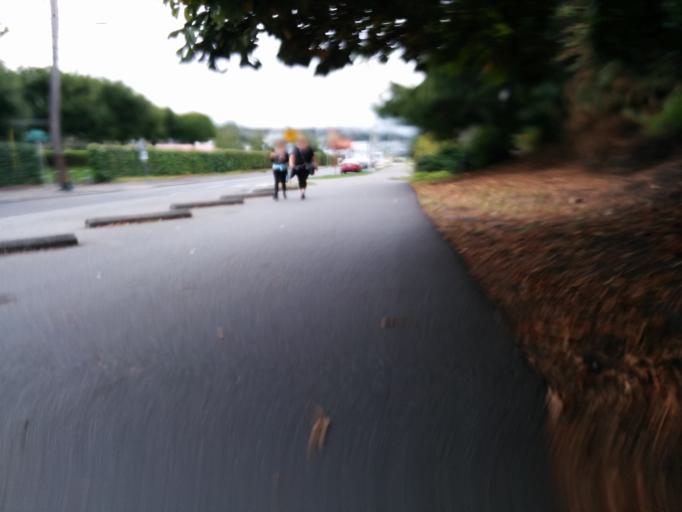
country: US
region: Washington
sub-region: King County
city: Seattle
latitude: 47.6470
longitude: -122.3359
